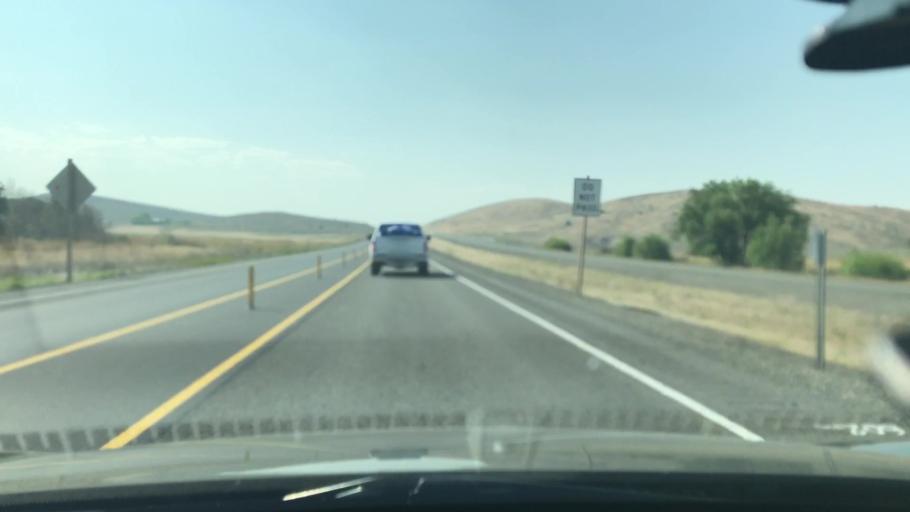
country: US
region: Oregon
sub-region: Baker County
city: Baker City
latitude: 44.6805
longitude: -117.6546
